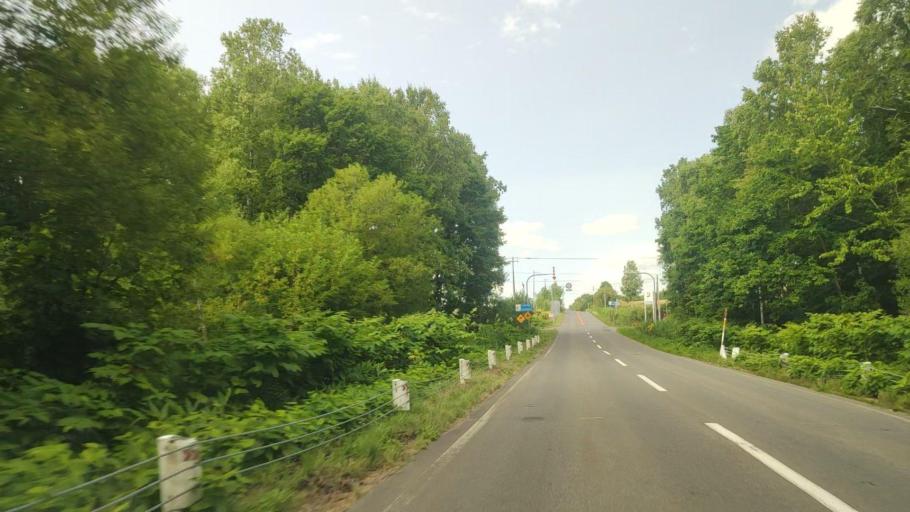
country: JP
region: Hokkaido
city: Nayoro
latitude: 44.2452
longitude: 142.4156
